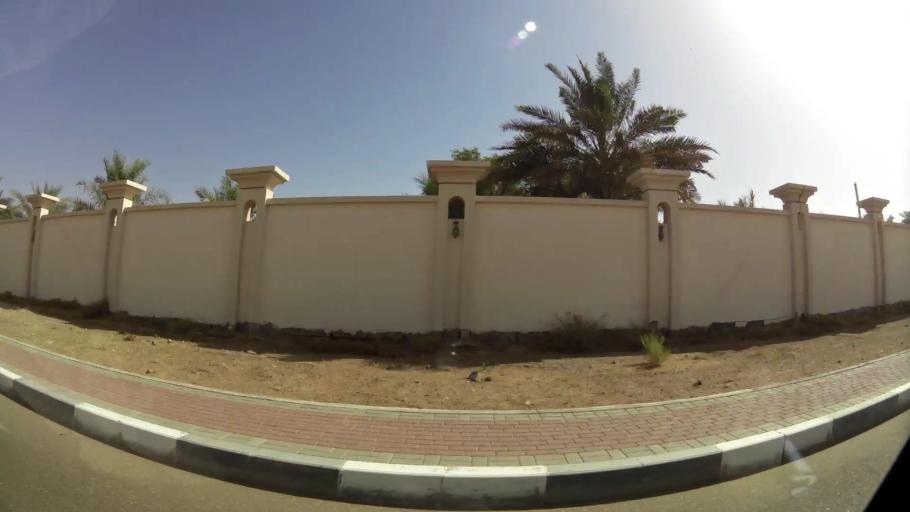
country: OM
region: Al Buraimi
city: Al Buraymi
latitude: 24.3390
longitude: 55.7929
